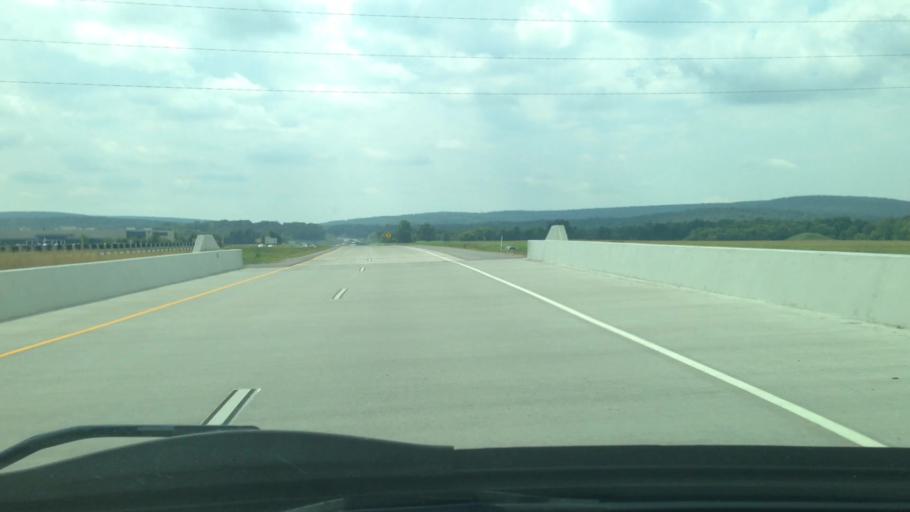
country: US
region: Wisconsin
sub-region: Sauk County
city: West Baraboo
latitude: 43.4601
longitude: -89.7782
